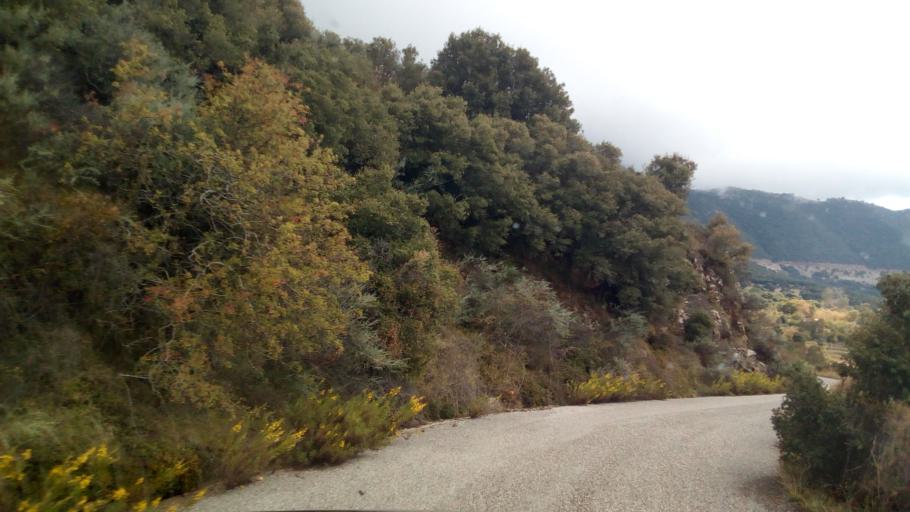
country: GR
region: West Greece
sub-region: Nomos Aitolias kai Akarnanias
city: Nafpaktos
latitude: 38.5002
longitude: 21.8377
